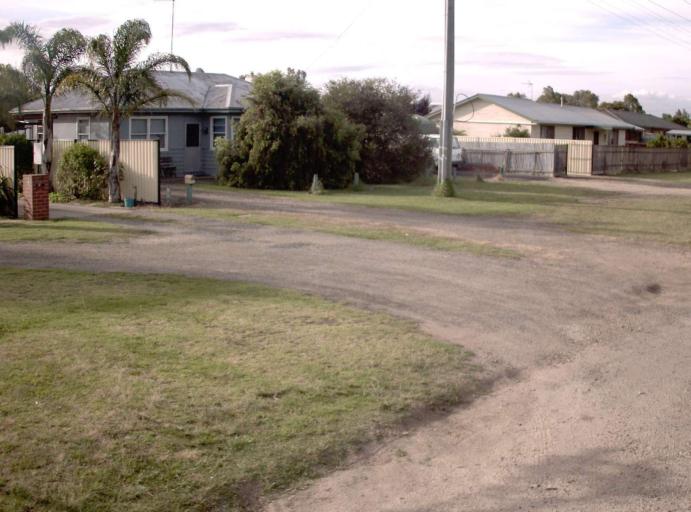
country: AU
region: Victoria
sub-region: Wellington
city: Sale
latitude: -37.9553
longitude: 146.9871
